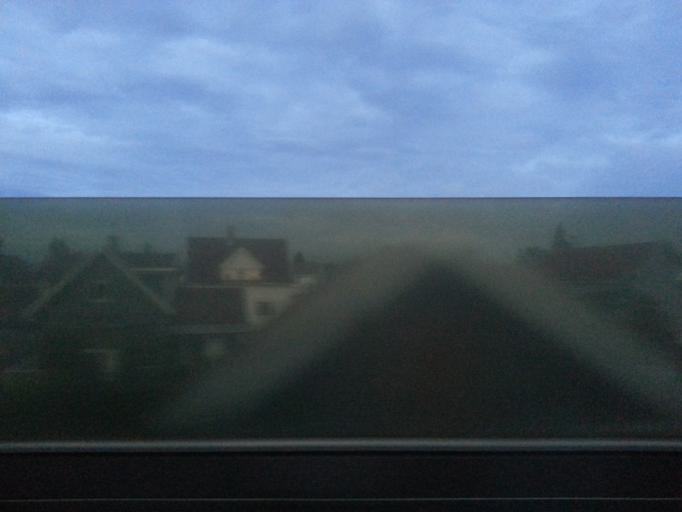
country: NO
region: Akershus
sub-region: Skedsmo
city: Lillestrom
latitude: 59.9563
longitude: 11.0563
